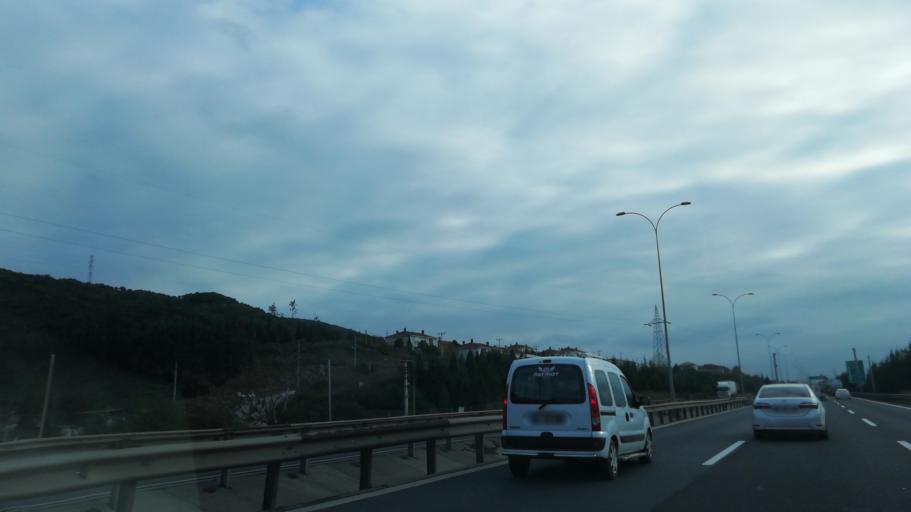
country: TR
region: Kocaeli
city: Korfez
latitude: 40.7754
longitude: 29.7570
